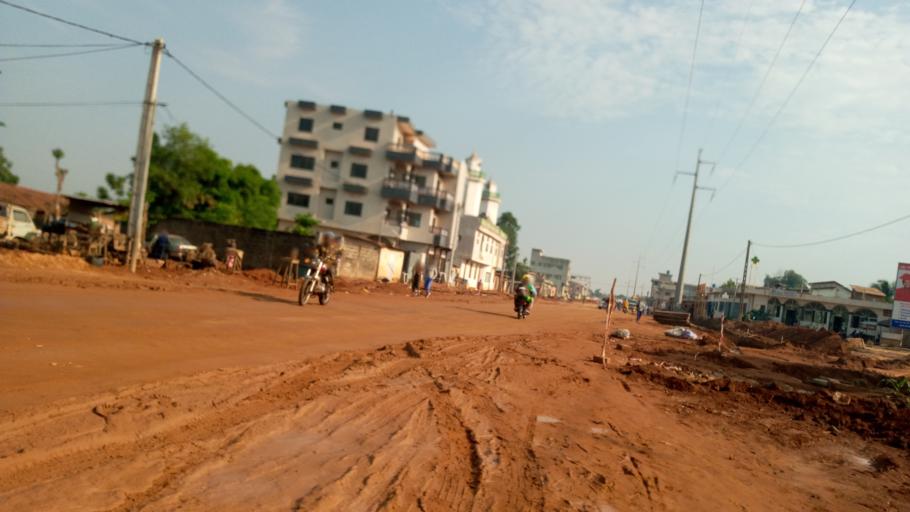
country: BJ
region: Queme
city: Porto-Novo
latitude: 6.4869
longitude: 2.6136
